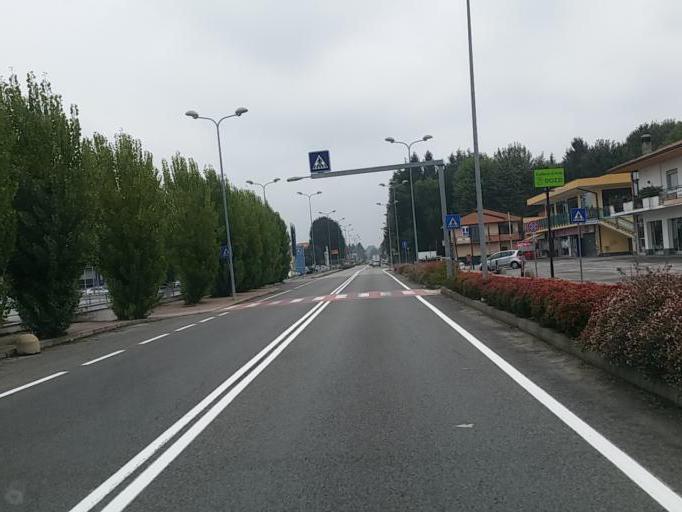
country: IT
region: Piedmont
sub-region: Provincia di Novara
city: Castelletto Sopra Ticino
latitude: 45.7196
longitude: 8.6131
